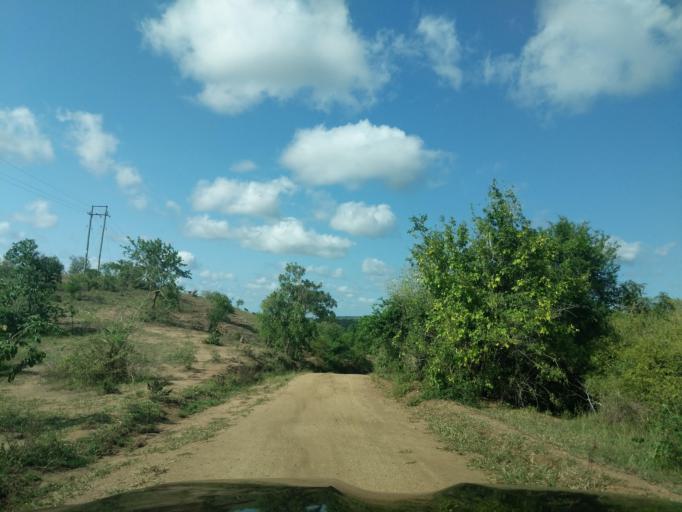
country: TZ
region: Tanga
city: Muheza
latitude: -5.4202
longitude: 38.6479
